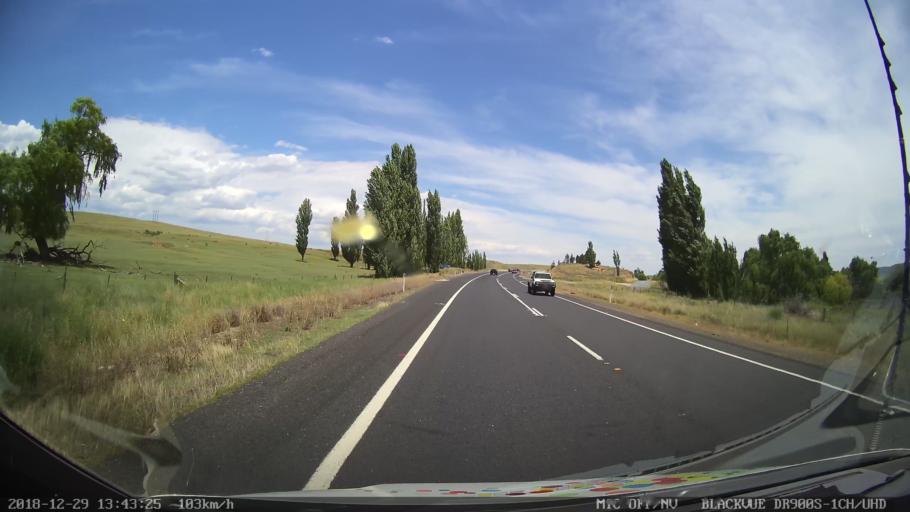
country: AU
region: New South Wales
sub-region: Cooma-Monaro
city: Cooma
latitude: -36.0721
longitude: 149.1598
